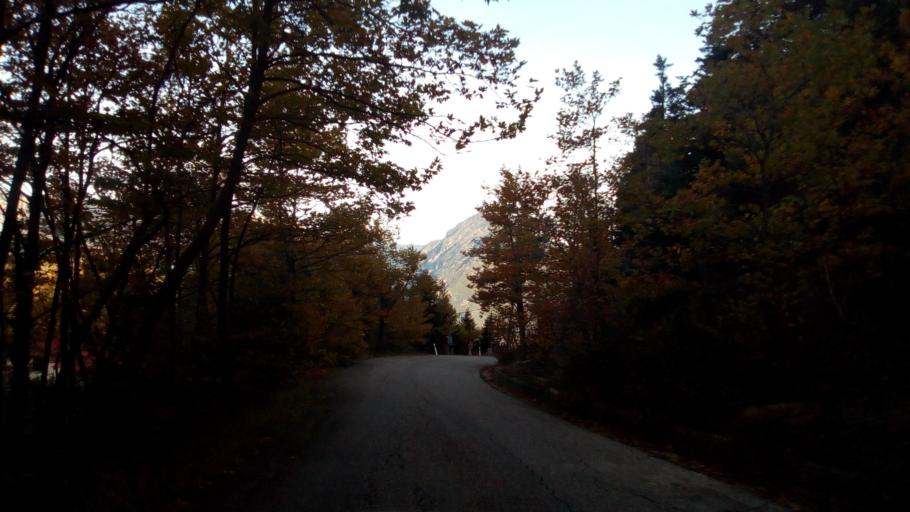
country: GR
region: West Greece
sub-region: Nomos Aitolias kai Akarnanias
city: Thermo
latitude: 38.6441
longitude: 21.8446
